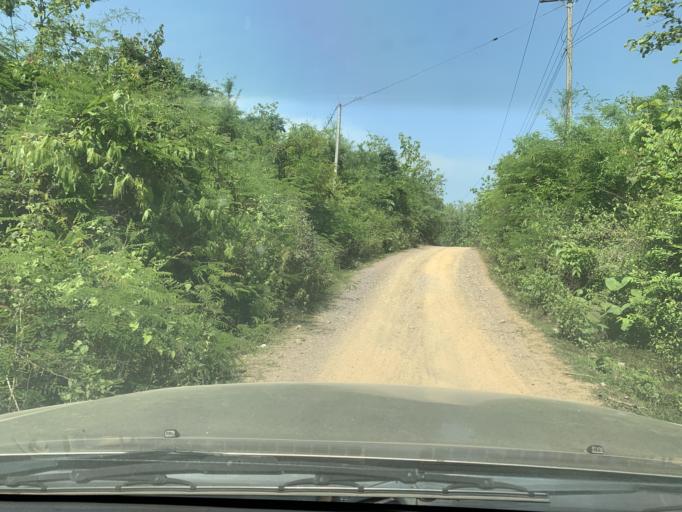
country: LA
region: Louangphabang
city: Louangphabang
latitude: 19.9159
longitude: 102.2672
